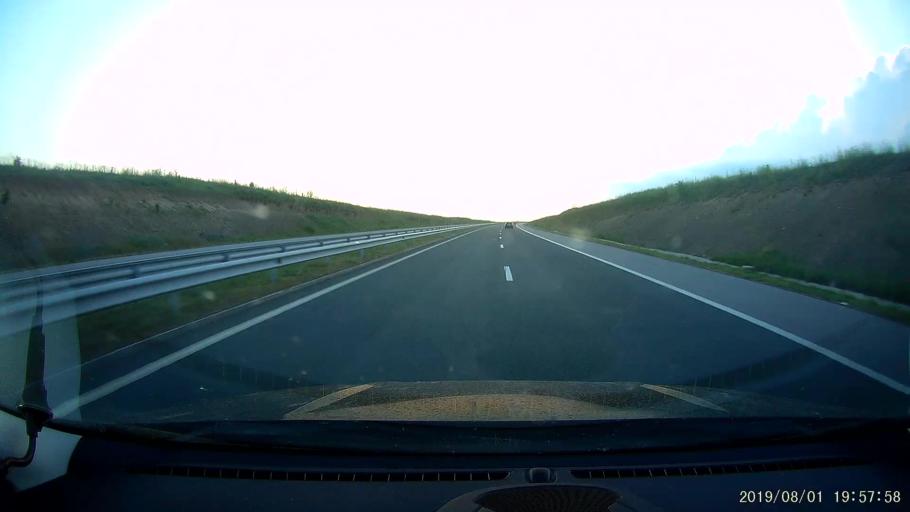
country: BG
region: Yambol
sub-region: Obshtina Straldzha
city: Straldzha
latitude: 42.5465
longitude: 26.7820
